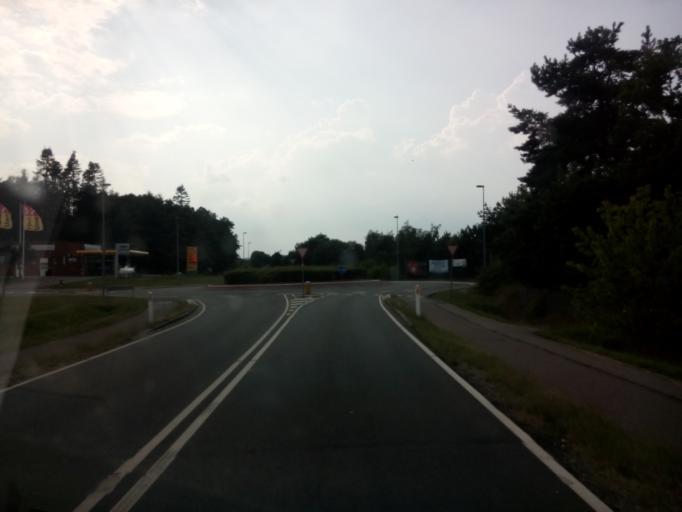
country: DK
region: Central Jutland
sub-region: Skanderborg Kommune
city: Ry
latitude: 56.0912
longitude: 9.7791
